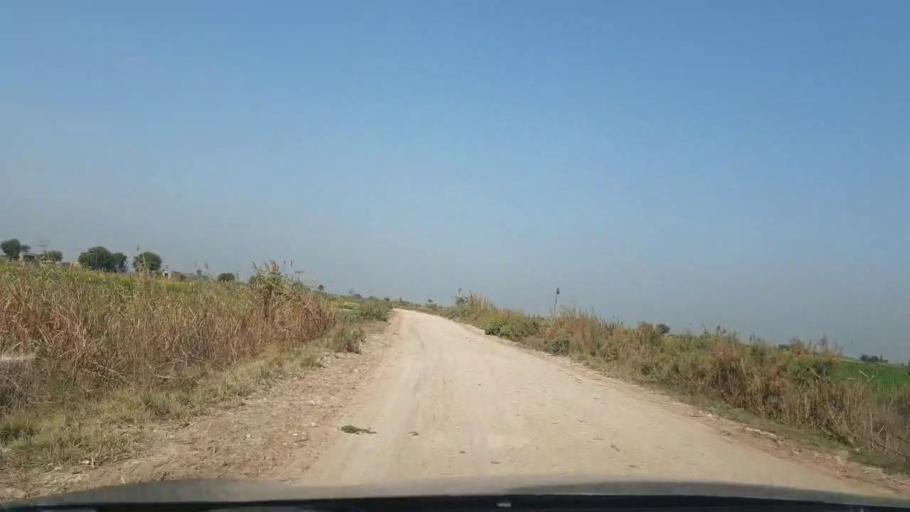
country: PK
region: Sindh
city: Berani
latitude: 25.7215
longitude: 68.8519
